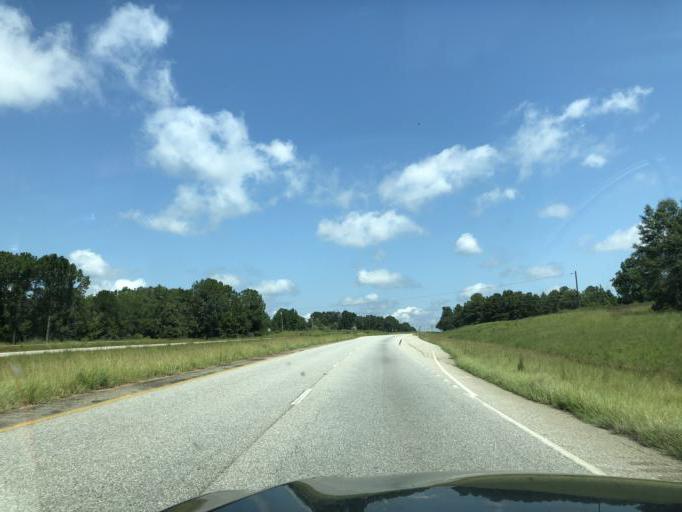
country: US
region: Alabama
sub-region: Henry County
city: Abbeville
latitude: 31.6972
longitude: -85.2783
